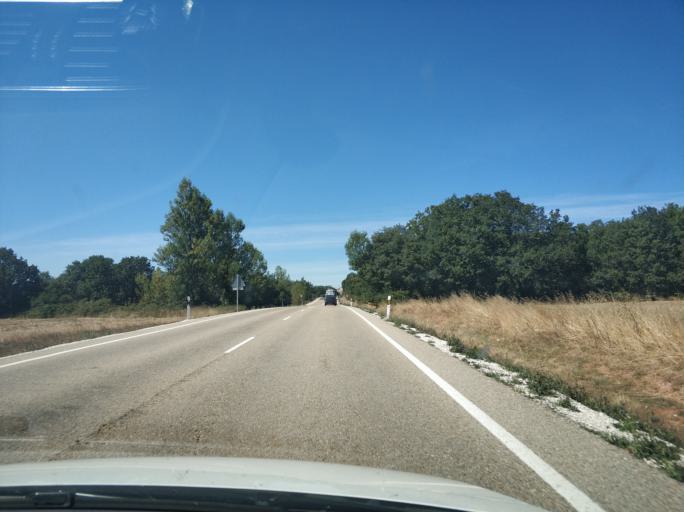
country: ES
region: Castille and Leon
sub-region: Provincia de Burgos
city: Montorio
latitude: 42.6285
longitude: -3.8559
